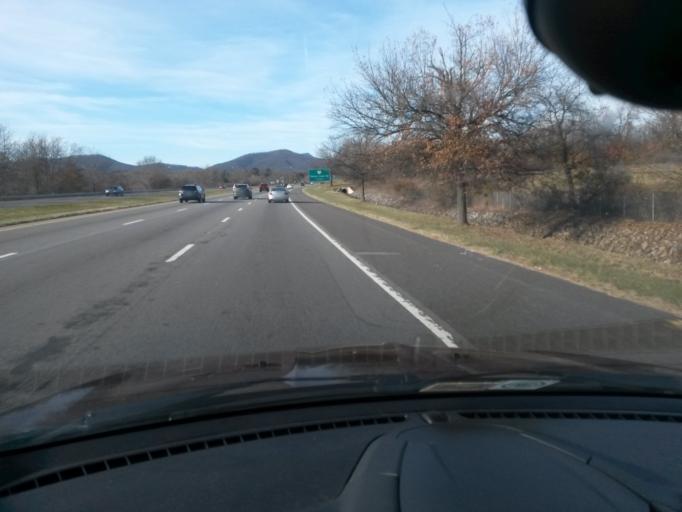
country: US
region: Virginia
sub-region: Roanoke County
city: Hollins
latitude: 37.3168
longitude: -79.9819
